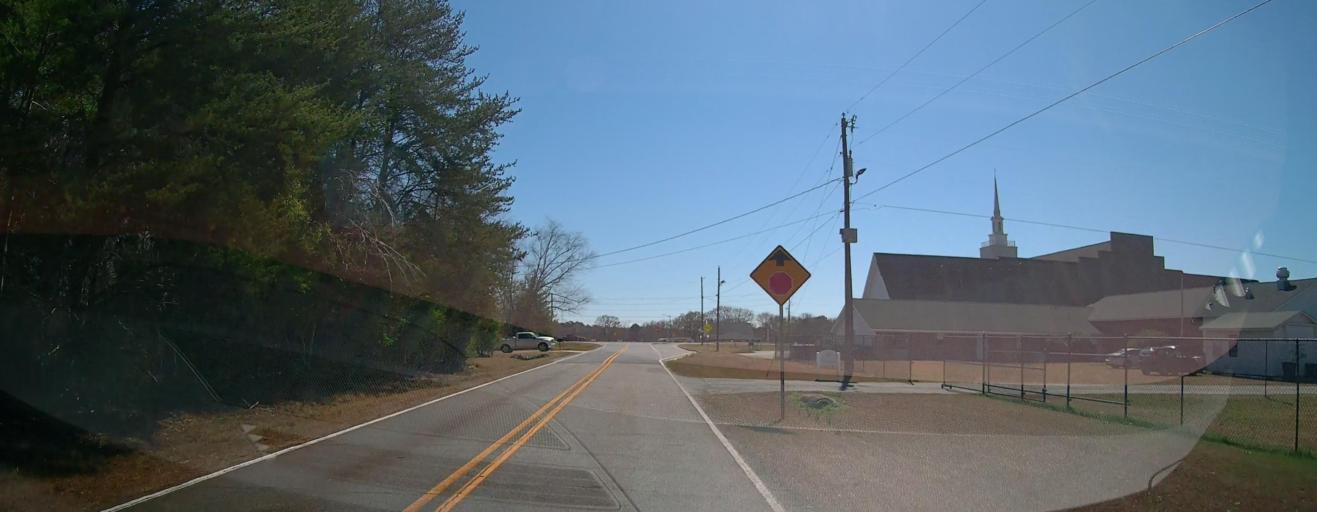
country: US
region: Georgia
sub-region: Houston County
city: Robins Air Force Base
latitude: 32.5559
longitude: -83.6367
